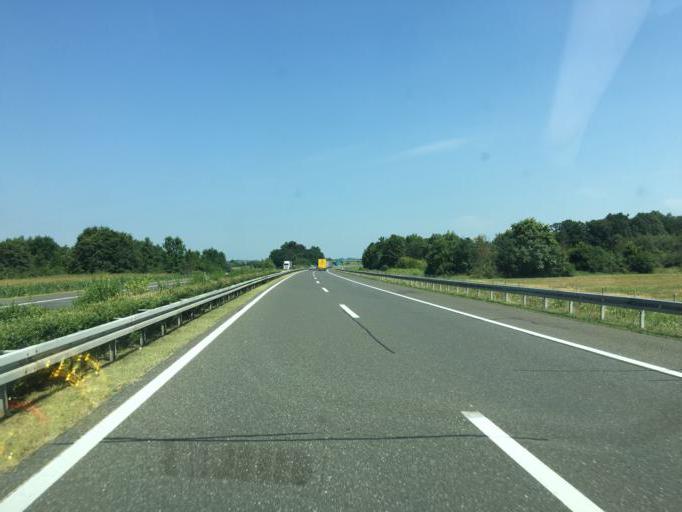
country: HR
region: Zagrebacka
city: Pojatno
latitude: 45.9046
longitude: 15.8204
